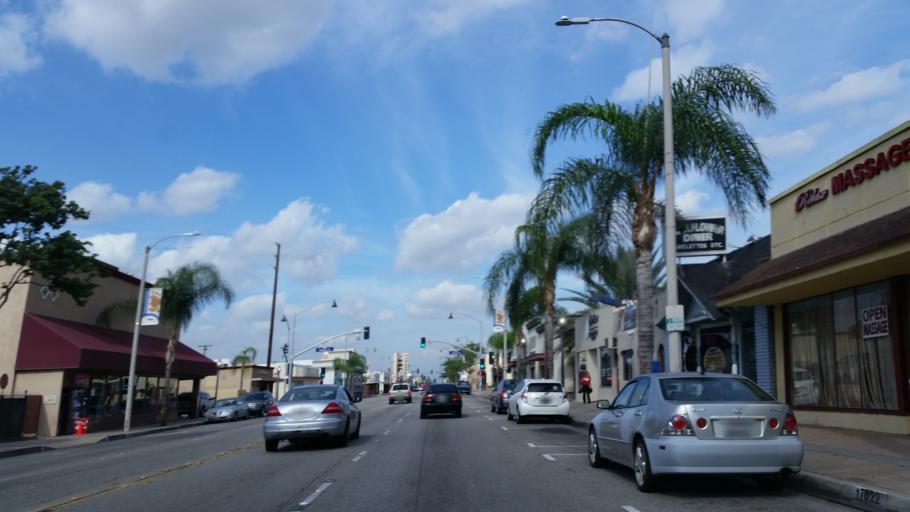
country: US
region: California
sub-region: Los Angeles County
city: Bellflower
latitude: 33.8794
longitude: -118.1252
